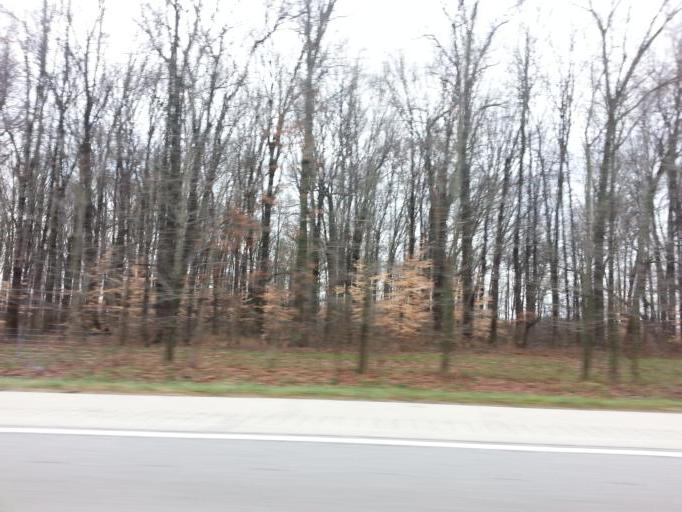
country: US
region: Indiana
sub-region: Decatur County
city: Greensburg
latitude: 39.3216
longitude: -85.3748
